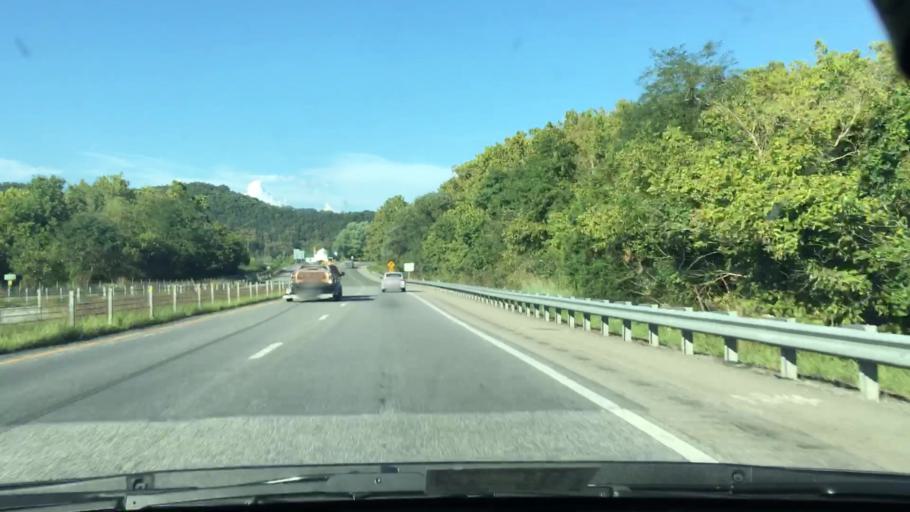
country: US
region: Virginia
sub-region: Alleghany County
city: Clifton Forge
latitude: 37.7996
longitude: -79.8719
